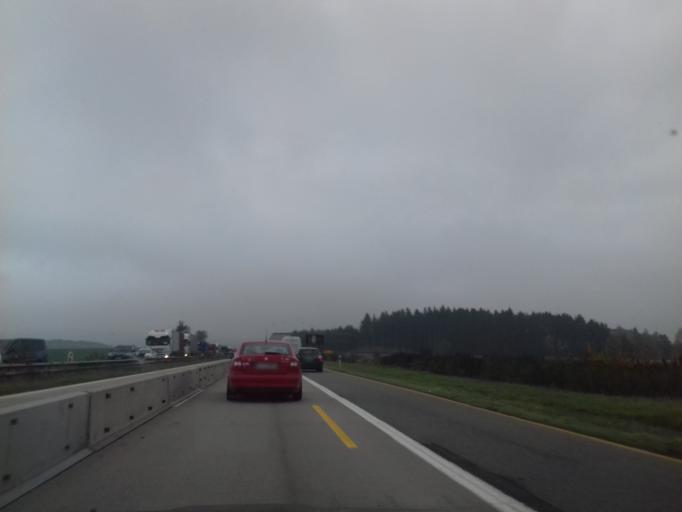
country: CZ
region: Vysocina
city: Dobronin
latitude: 49.4391
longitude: 15.6384
